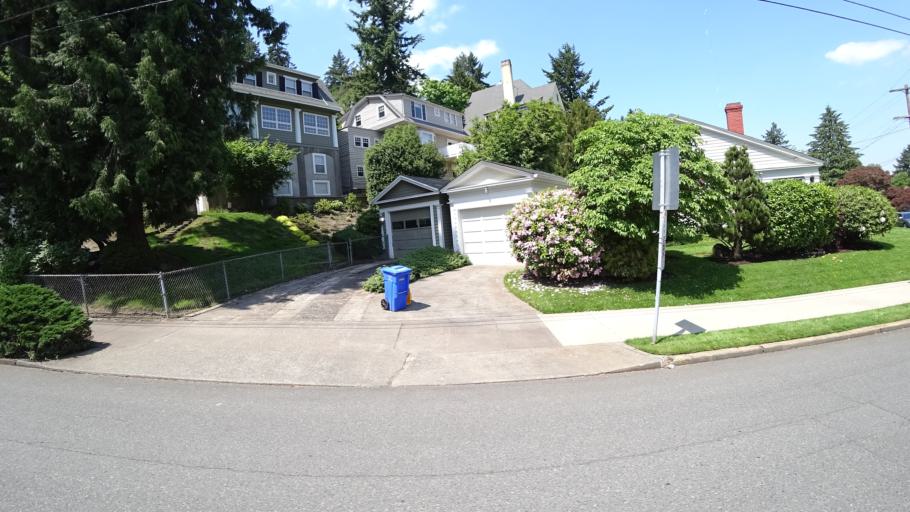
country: US
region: Oregon
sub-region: Multnomah County
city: Portland
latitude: 45.5213
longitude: -122.7071
